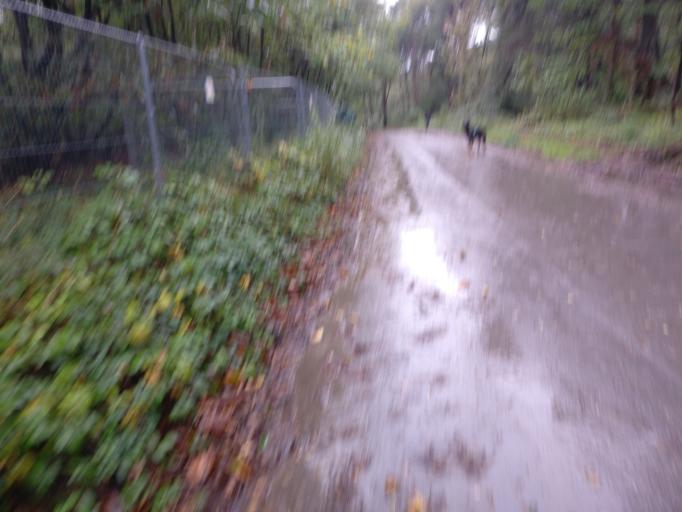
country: GB
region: England
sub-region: Surrey
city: Frimley
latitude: 51.3142
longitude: -0.7023
